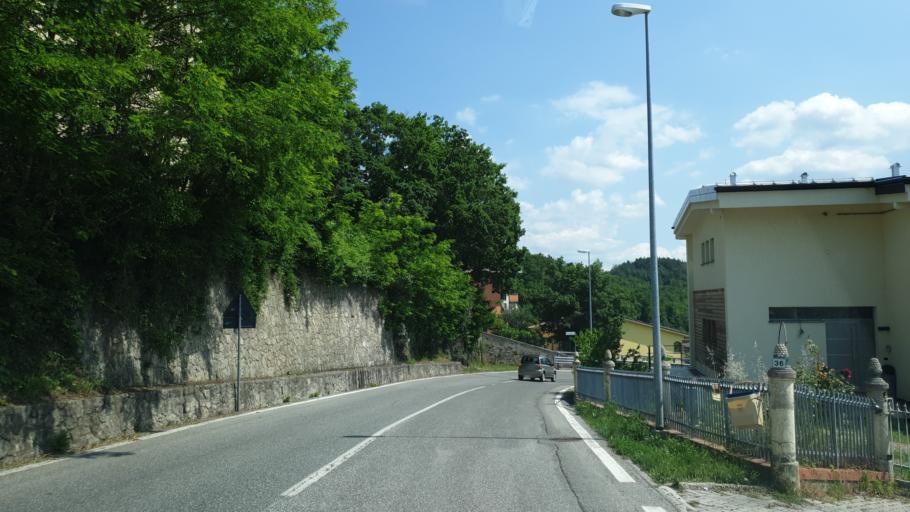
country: SM
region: San Marino
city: San Marino
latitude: 43.9350
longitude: 12.4378
